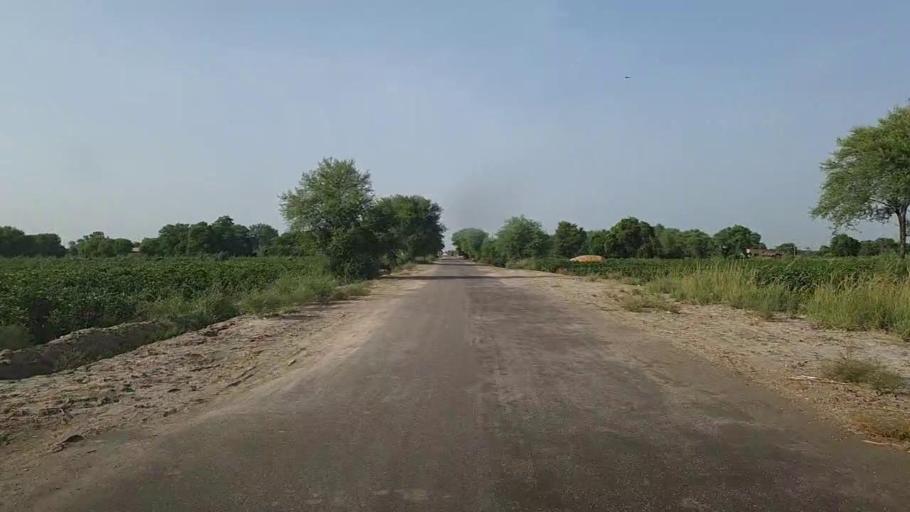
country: PK
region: Sindh
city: Ubauro
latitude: 28.0902
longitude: 69.8442
